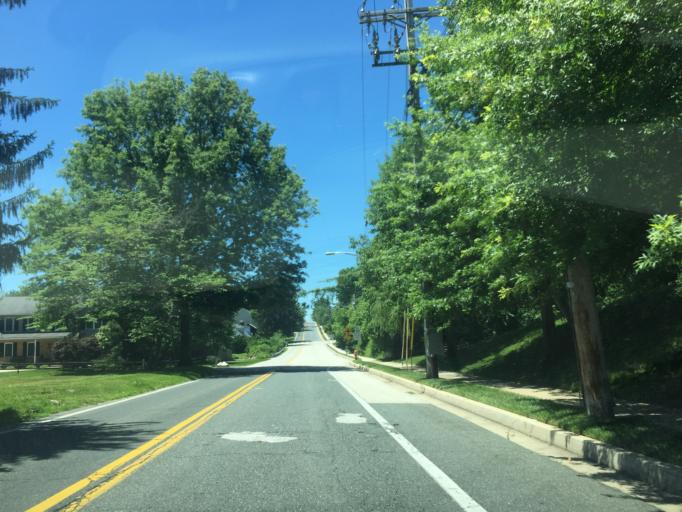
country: US
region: Maryland
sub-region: Baltimore County
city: Garrison
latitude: 39.3904
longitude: -76.7431
